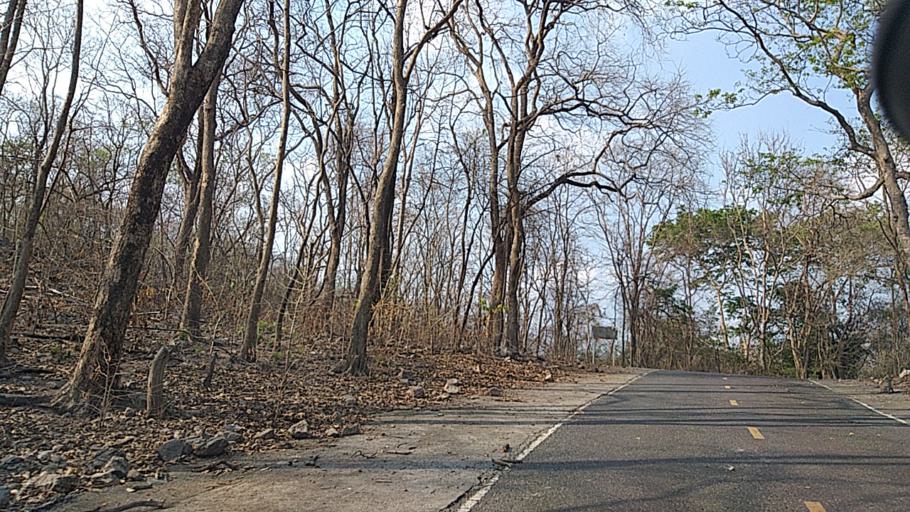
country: TH
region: Sara Buri
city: Saraburi
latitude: 14.4623
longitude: 100.9487
